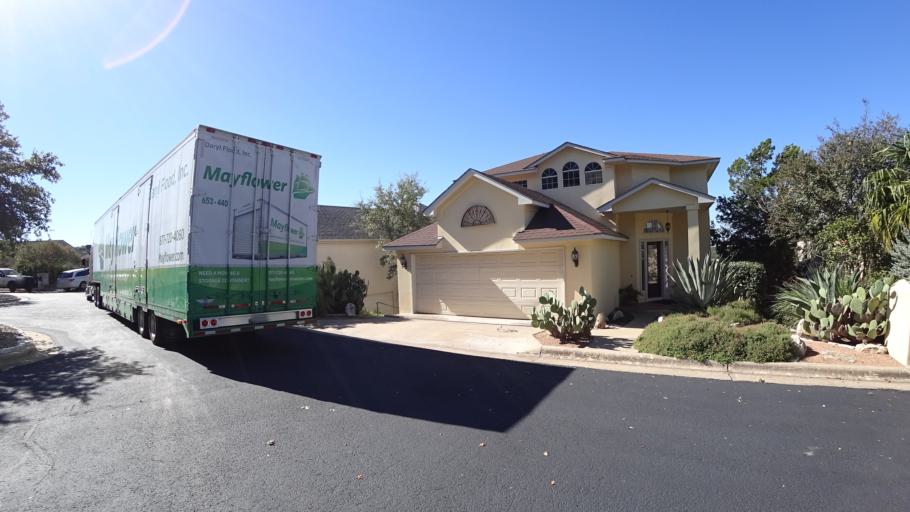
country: US
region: Texas
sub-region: Travis County
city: West Lake Hills
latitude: 30.3597
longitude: -97.7770
